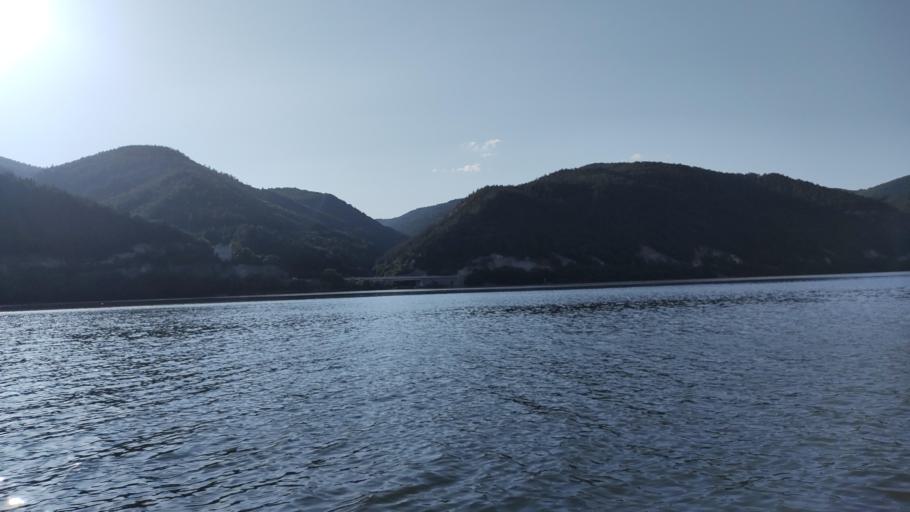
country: RO
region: Mehedinti
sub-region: Comuna Svinita
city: Svinita
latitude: 44.5260
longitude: 22.2090
